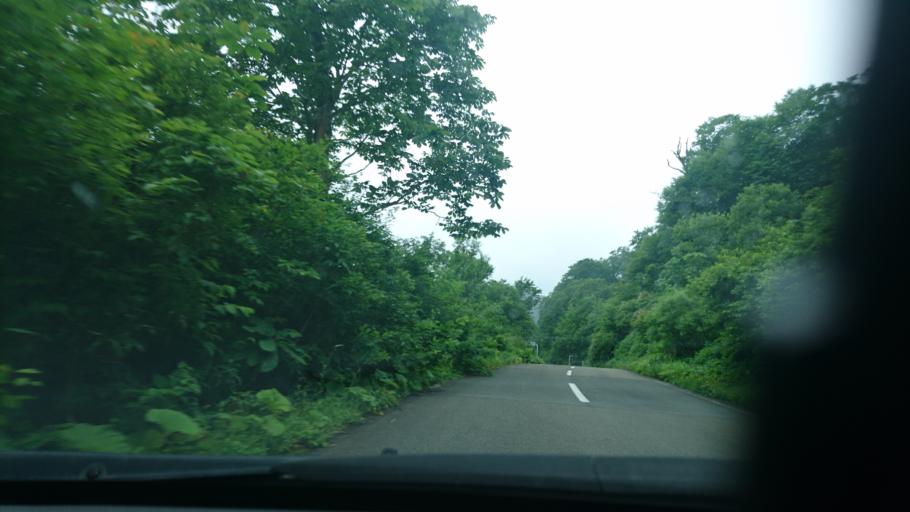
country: JP
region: Akita
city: Yuzawa
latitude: 39.1423
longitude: 140.7690
